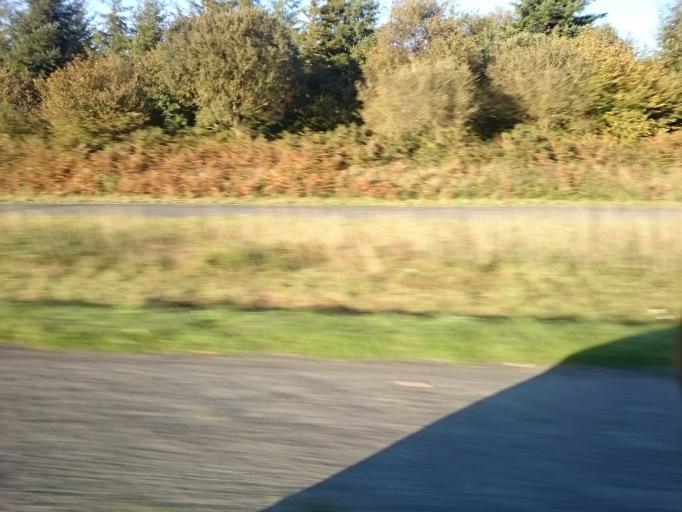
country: FR
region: Brittany
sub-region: Departement des Cotes-d'Armor
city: Lanrodec
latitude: 48.5395
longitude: -3.0661
